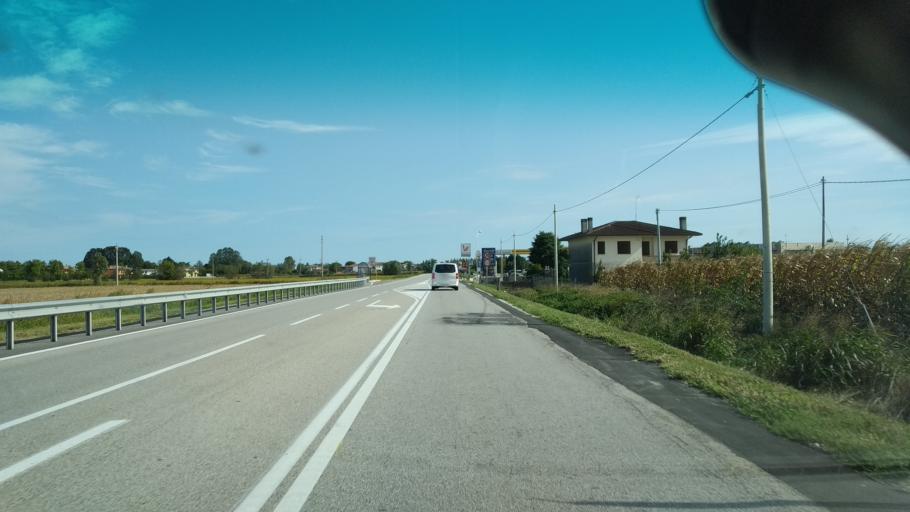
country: IT
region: Veneto
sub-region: Provincia di Padova
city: Vallonga
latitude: 45.2808
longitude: 12.0825
